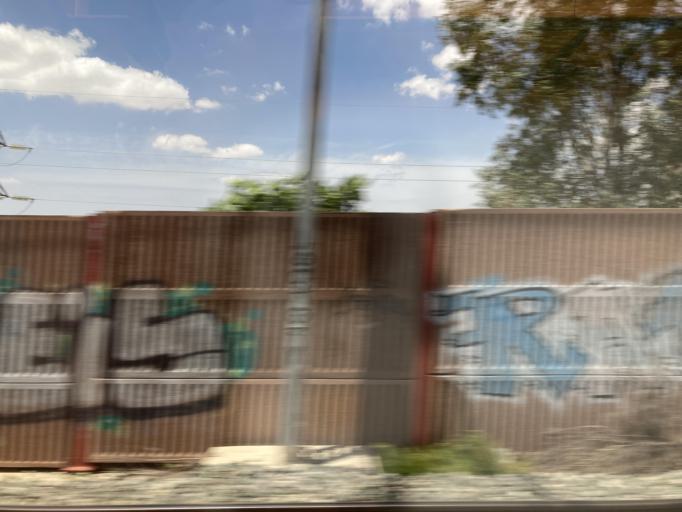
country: ES
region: Andalusia
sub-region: Provincia de Cadiz
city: Jerez de la Frontera
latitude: 36.6699
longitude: -6.1237
